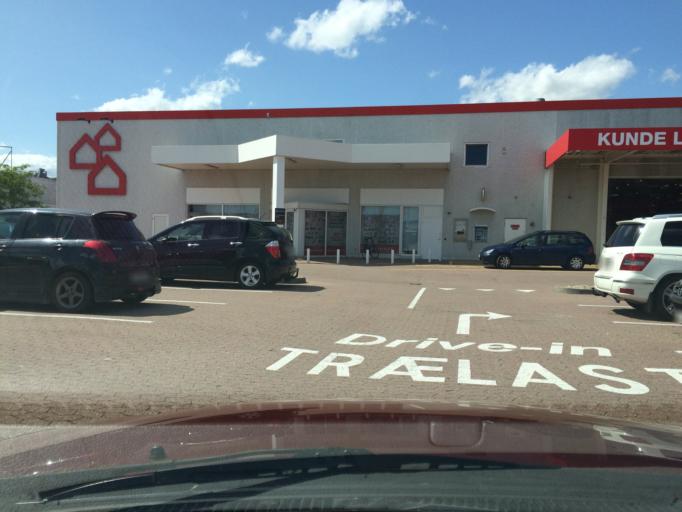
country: DK
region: Central Jutland
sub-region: Arhus Kommune
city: Stavtrup
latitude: 56.1833
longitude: 10.1008
